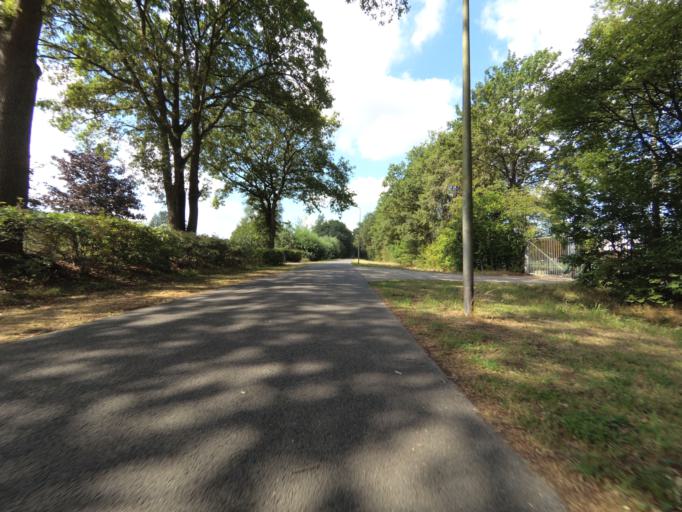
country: NL
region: Overijssel
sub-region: Gemeente Oldenzaal
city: Oldenzaal
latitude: 52.3075
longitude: 6.9055
